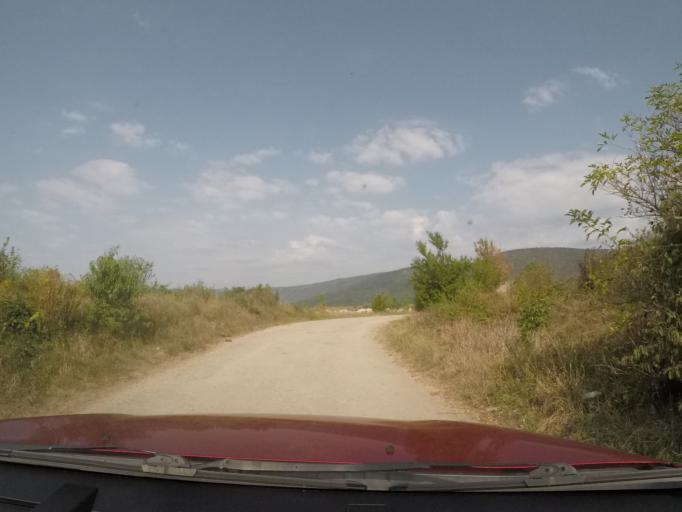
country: SK
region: Kosicky
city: Moldava nad Bodvou
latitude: 48.6080
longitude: 20.9441
